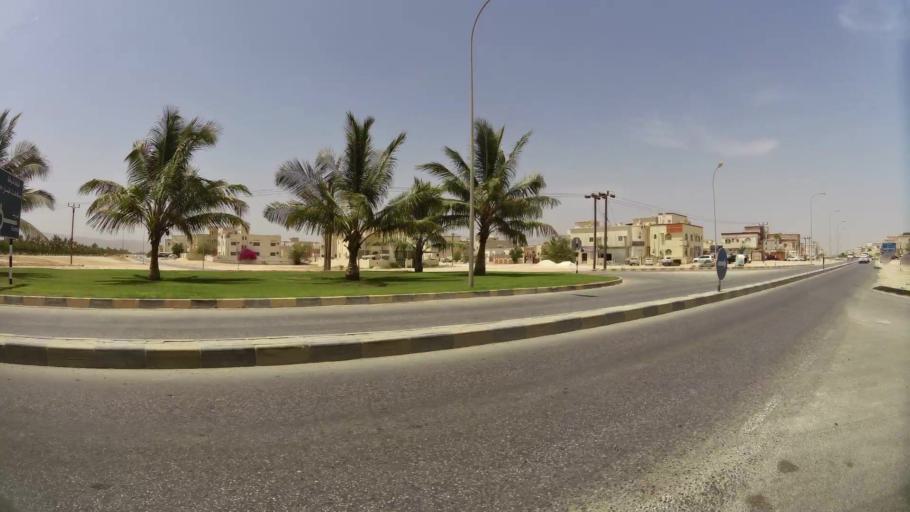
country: OM
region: Zufar
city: Salalah
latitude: 17.0684
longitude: 54.1480
